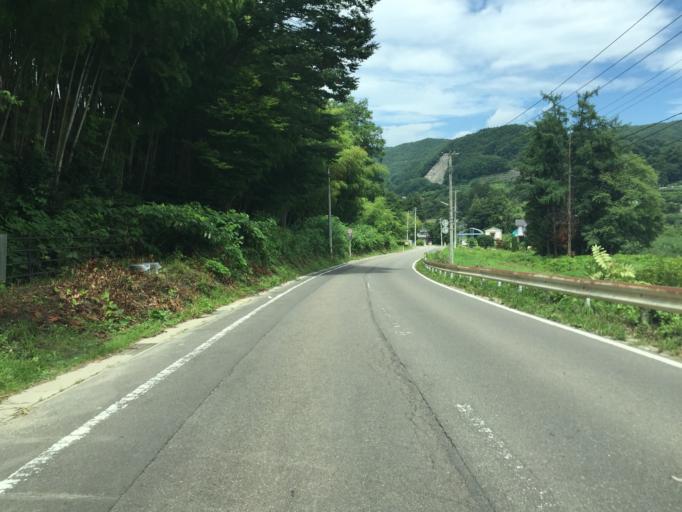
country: JP
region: Fukushima
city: Fukushima-shi
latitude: 37.8207
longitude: 140.4155
